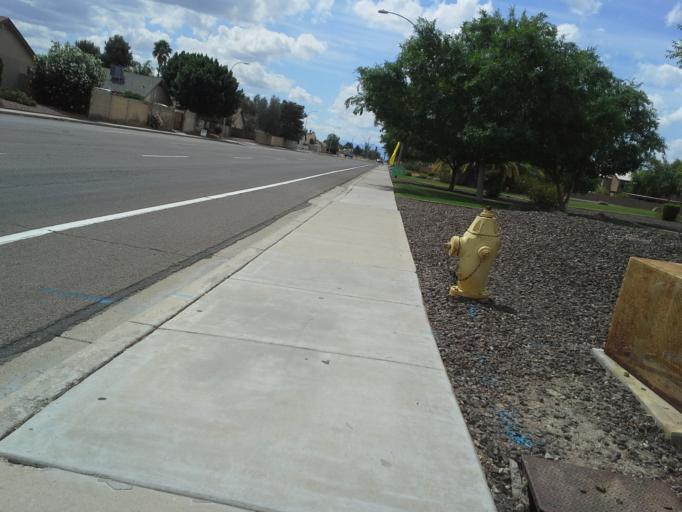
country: US
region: Arizona
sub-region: Maricopa County
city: Peoria
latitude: 33.6132
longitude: -112.2289
